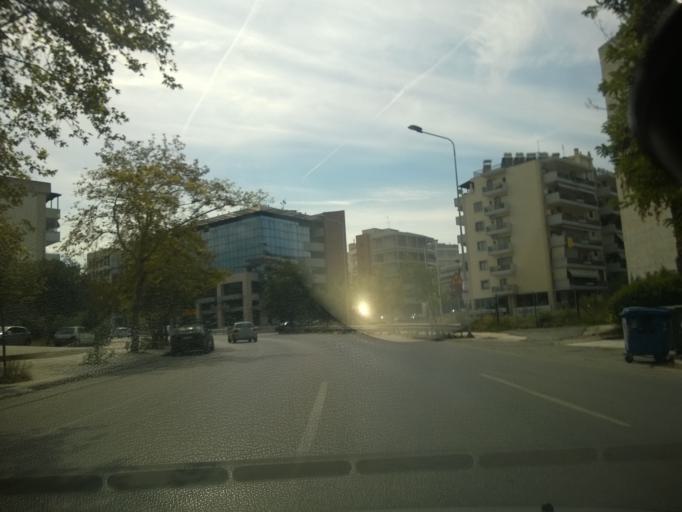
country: GR
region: Central Macedonia
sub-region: Nomos Thessalonikis
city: Kalamaria
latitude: 40.5881
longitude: 22.9542
